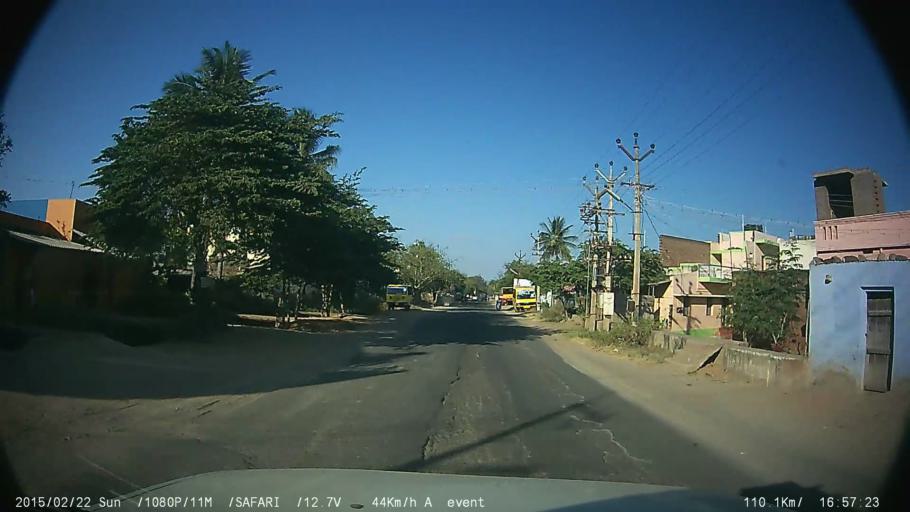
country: IN
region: Tamil Nadu
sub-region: Theni
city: Gudalur
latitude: 9.6828
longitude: 77.2461
